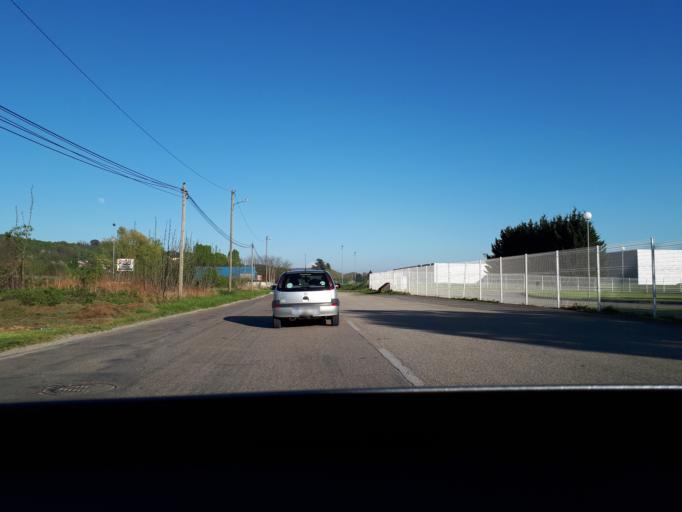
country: FR
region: Rhone-Alpes
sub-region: Departement de l'Isere
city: Bourgoin-Jallieu
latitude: 45.6020
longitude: 5.2598
